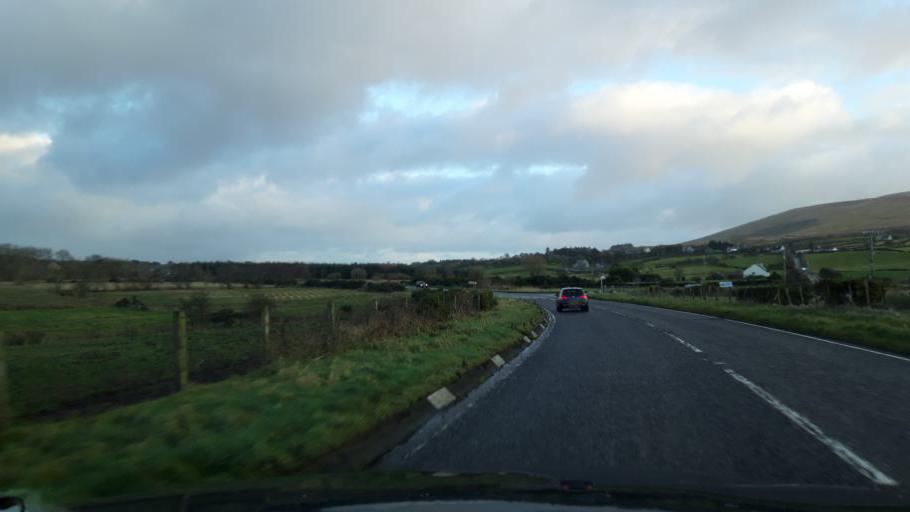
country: GB
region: Northern Ireland
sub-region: Moyle District
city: Ballycastle
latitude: 55.1466
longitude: -6.3119
